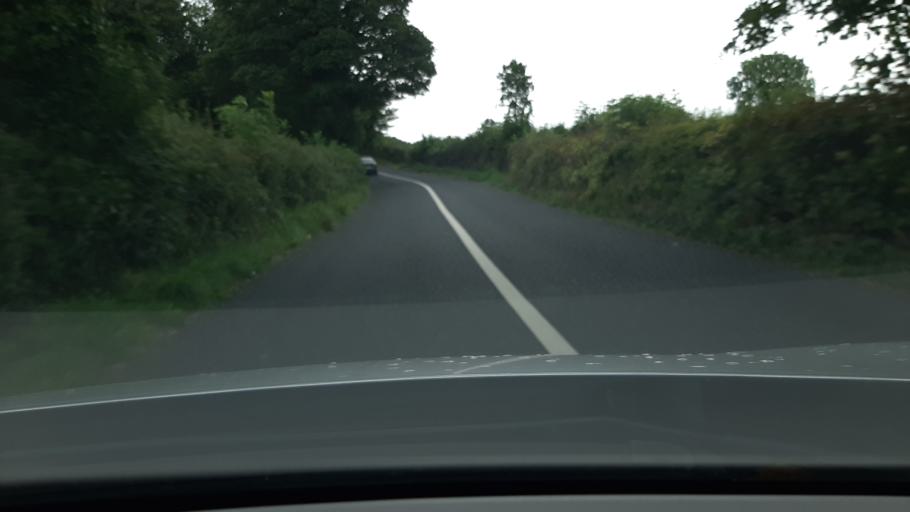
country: IE
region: Leinster
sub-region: Kildare
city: Rathangan
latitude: 53.2123
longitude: -6.9661
